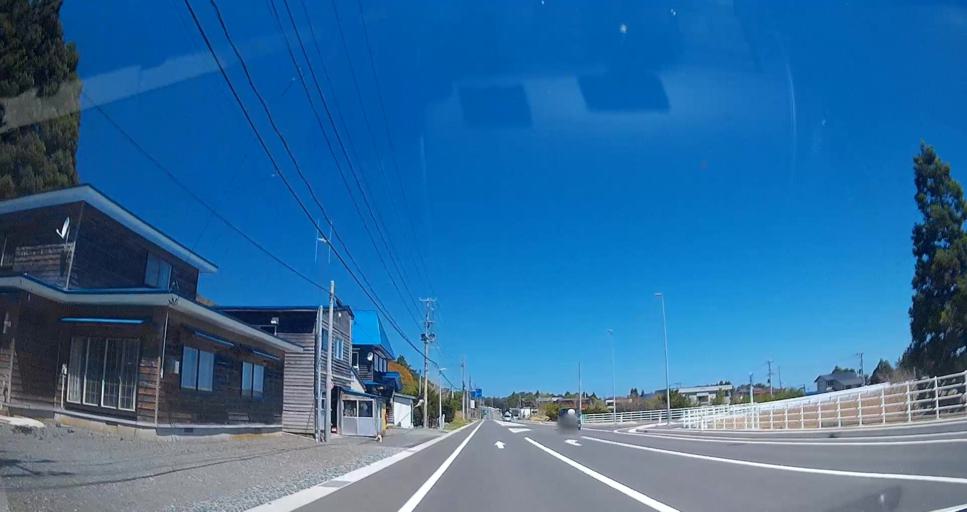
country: JP
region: Aomori
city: Mutsu
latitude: 41.1088
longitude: 141.3904
